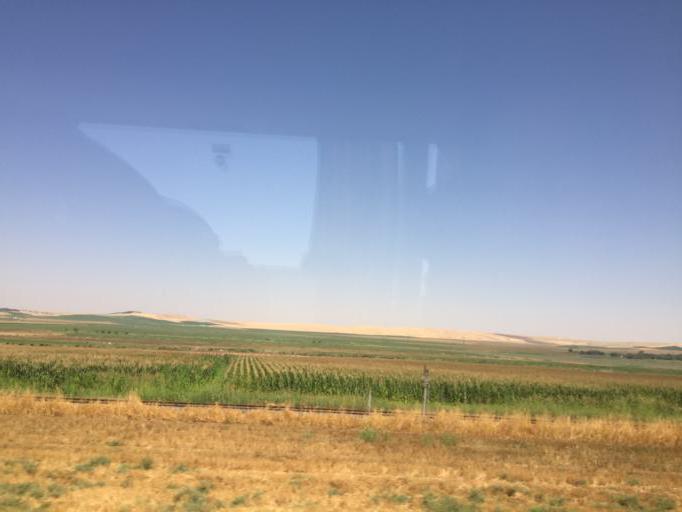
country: TR
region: Diyarbakir
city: Tepe
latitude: 37.8494
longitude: 40.7901
